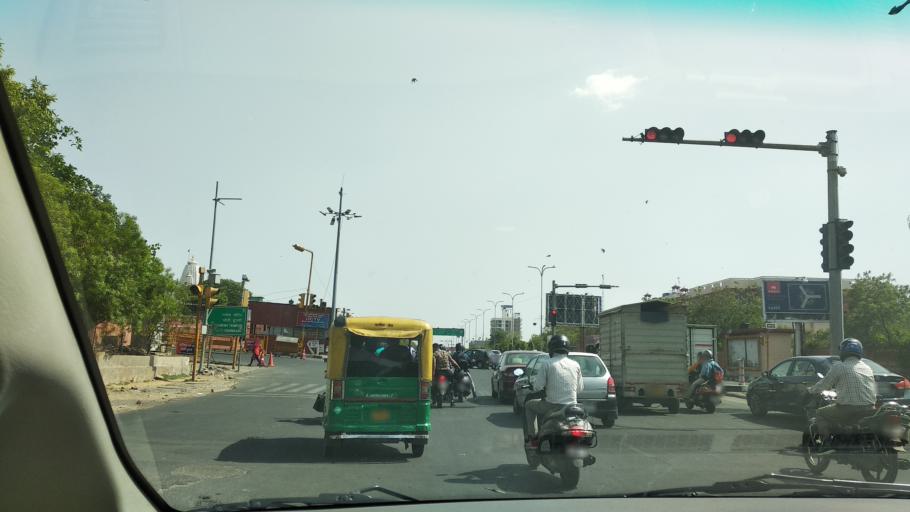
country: IN
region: Rajasthan
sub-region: Jaipur
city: Jaipur
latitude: 26.8952
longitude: 75.8153
